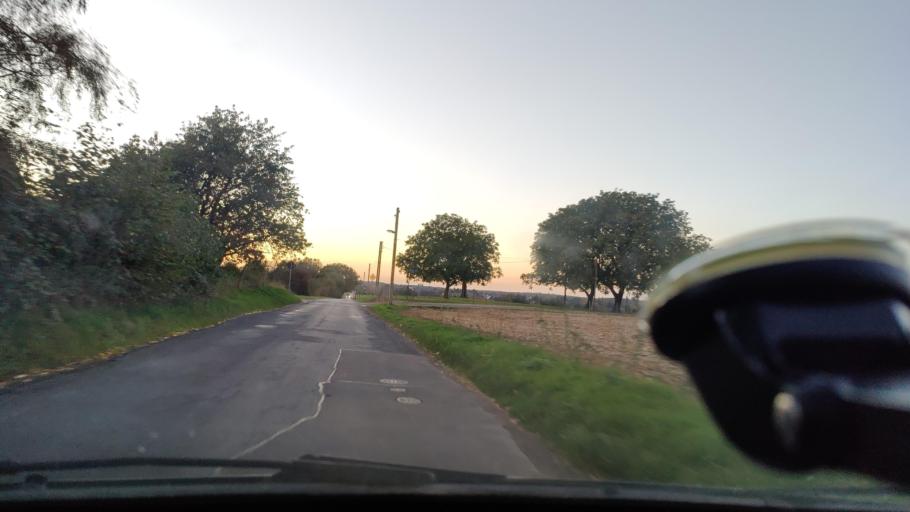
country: DE
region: North Rhine-Westphalia
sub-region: Regierungsbezirk Dusseldorf
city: Goch
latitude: 51.7101
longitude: 6.1942
